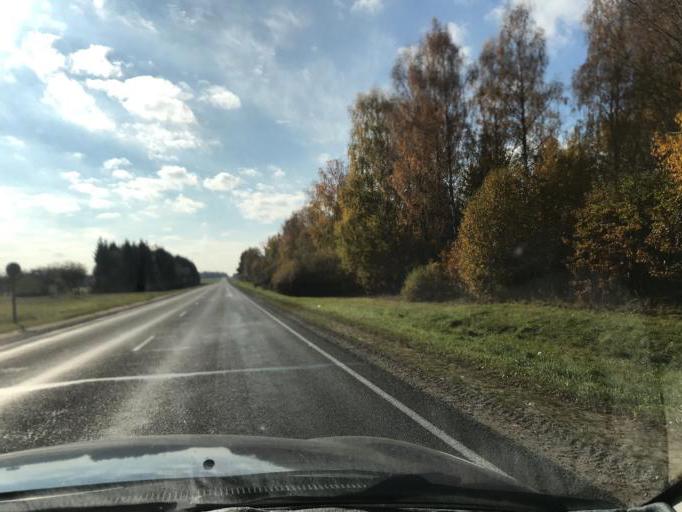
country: BY
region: Grodnenskaya
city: Voranava
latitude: 54.2053
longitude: 25.3494
